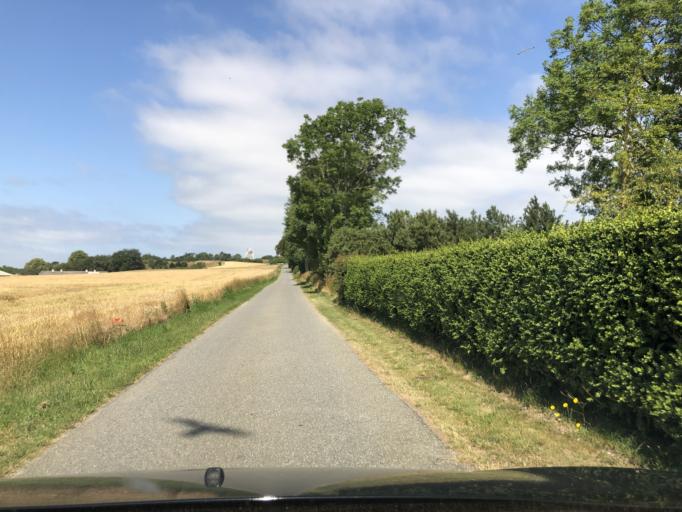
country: DK
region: South Denmark
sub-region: AEro Kommune
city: AEroskobing
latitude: 54.9195
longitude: 10.2902
